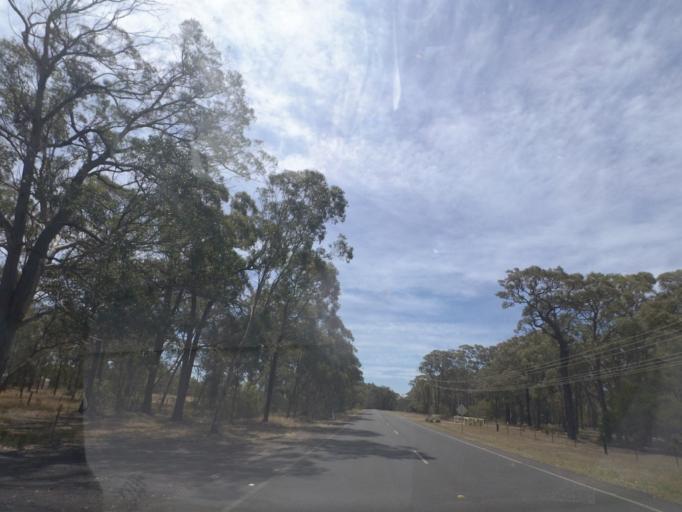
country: AU
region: New South Wales
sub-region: Wollondilly
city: Buxton
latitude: -34.3175
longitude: 150.5770
